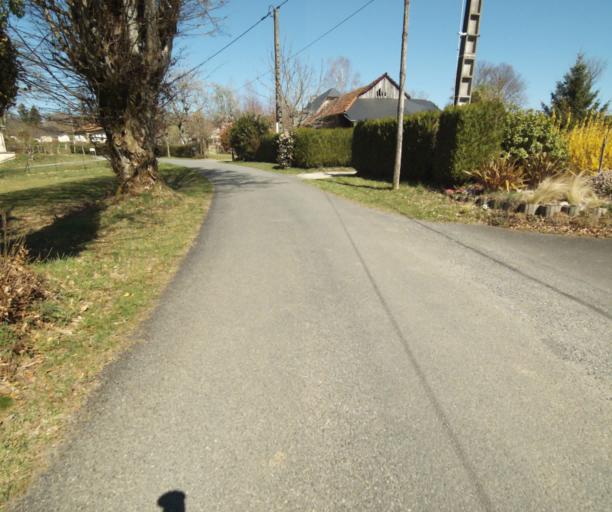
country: FR
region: Limousin
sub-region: Departement de la Correze
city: Saint-Clement
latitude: 45.3384
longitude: 1.6951
